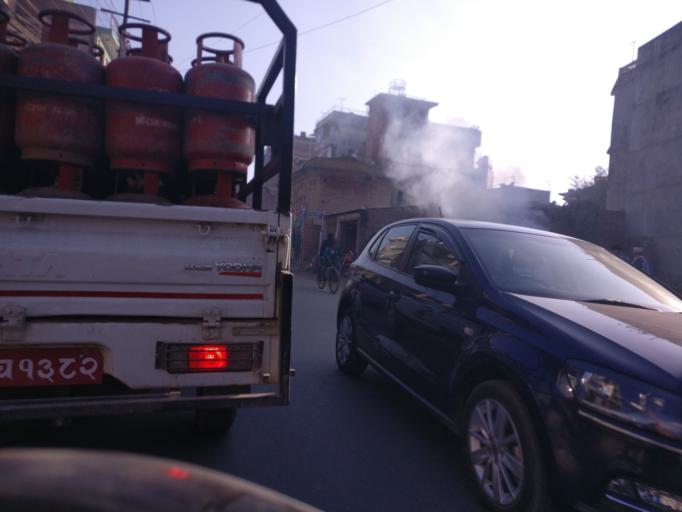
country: NP
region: Central Region
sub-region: Bagmati Zone
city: Patan
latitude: 27.6606
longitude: 85.3239
